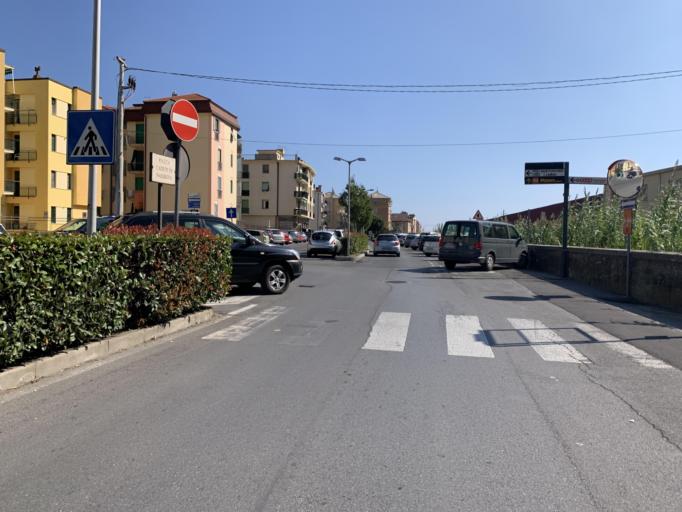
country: IT
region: Liguria
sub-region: Provincia di Savona
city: Finale Ligure
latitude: 44.1703
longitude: 8.3362
